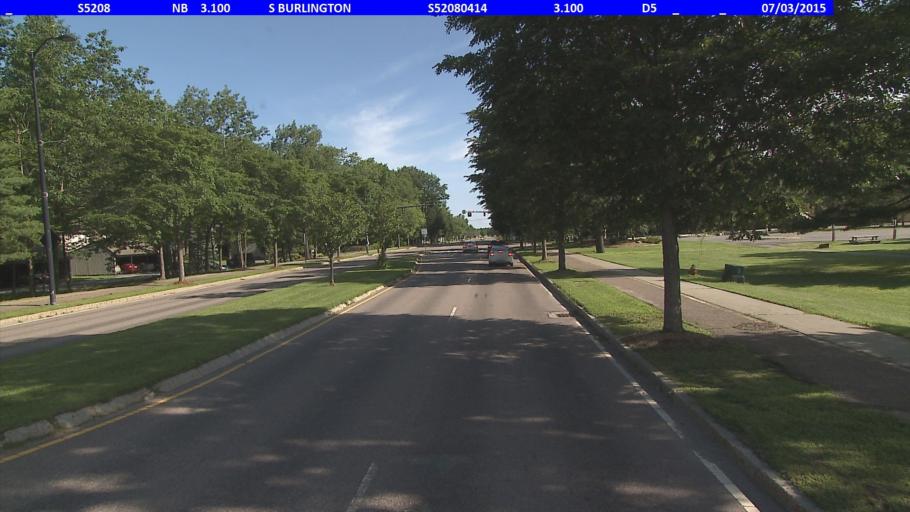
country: US
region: Vermont
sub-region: Chittenden County
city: South Burlington
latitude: 44.4549
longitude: -73.1790
